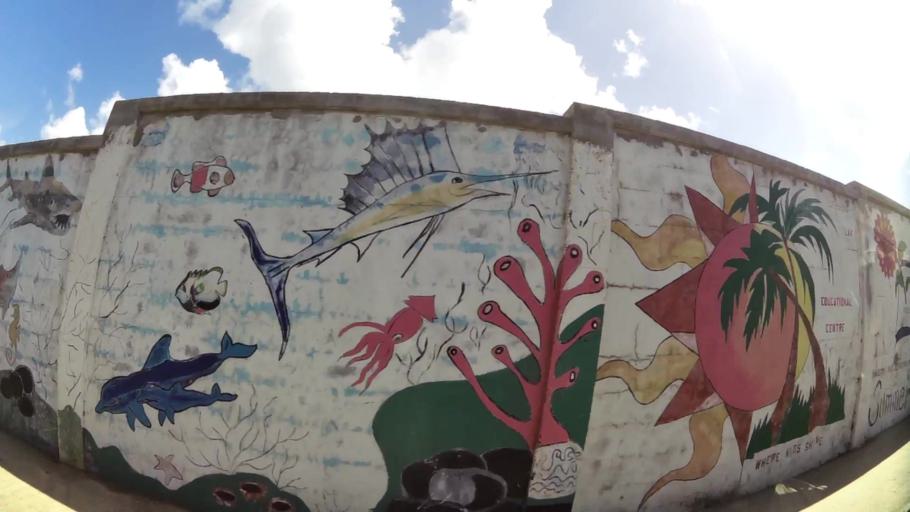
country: VG
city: Tortola
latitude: 18.4387
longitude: -64.4381
